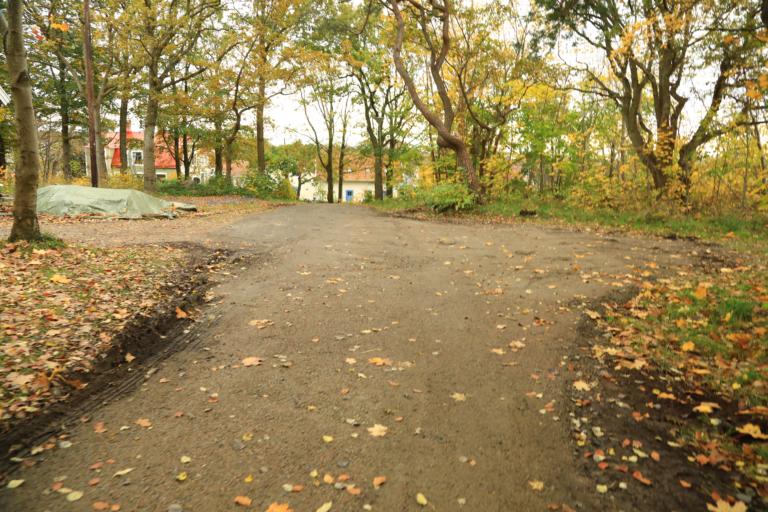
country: SE
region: Halland
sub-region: Varbergs Kommun
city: Varberg
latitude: 57.1000
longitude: 12.2587
